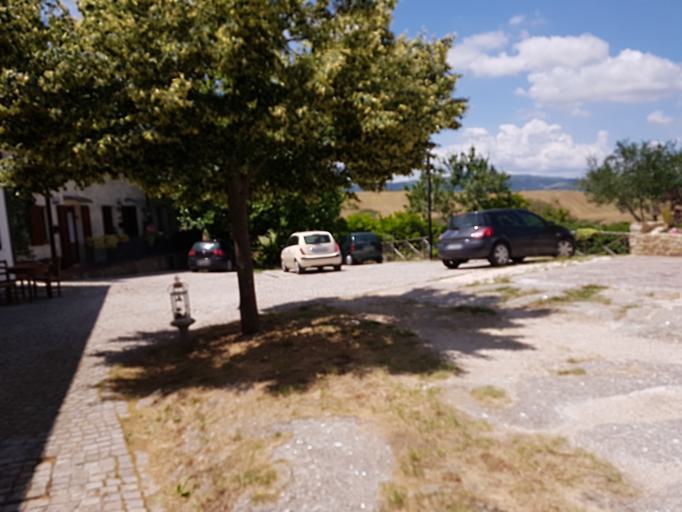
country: IT
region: The Marches
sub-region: Provincia di Pesaro e Urbino
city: Sassofeltrio
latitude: 43.8723
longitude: 12.5453
